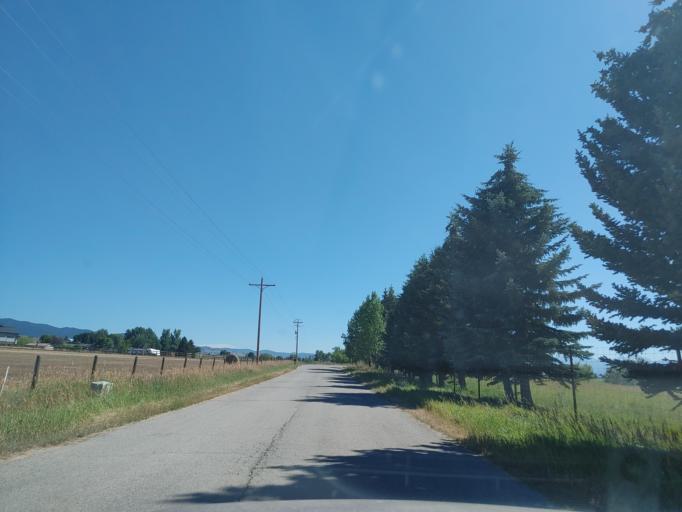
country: US
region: Montana
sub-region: Ravalli County
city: Hamilton
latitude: 46.3467
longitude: -114.0615
